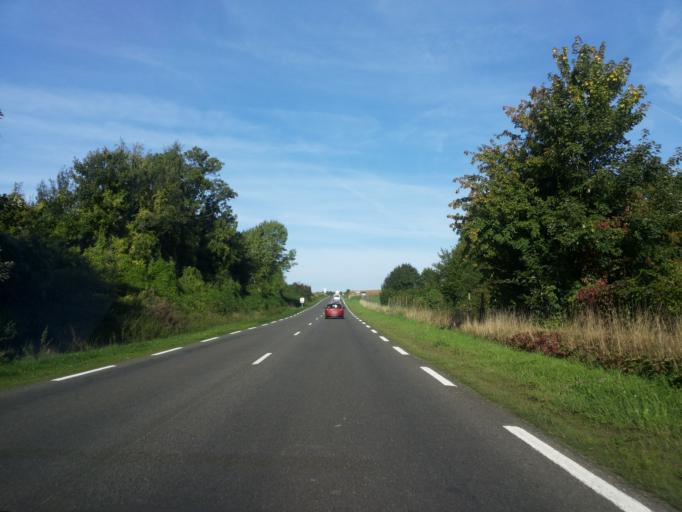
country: FR
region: Picardie
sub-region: Departement de l'Aisne
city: Charmes
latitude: 49.6351
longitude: 3.4112
